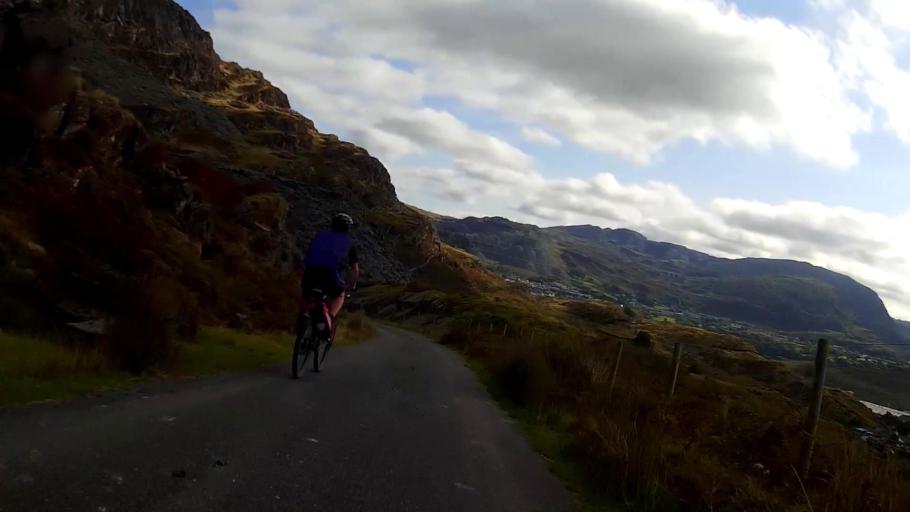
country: GB
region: Wales
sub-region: Gwynedd
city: Blaenau-Ffestiniog
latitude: 52.9884
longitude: -3.9704
